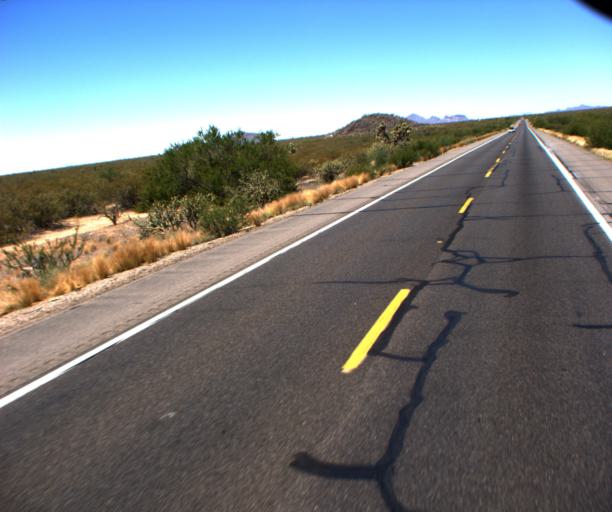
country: US
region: Arizona
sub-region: Yavapai County
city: Congress
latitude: 34.1667
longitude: -113.0128
